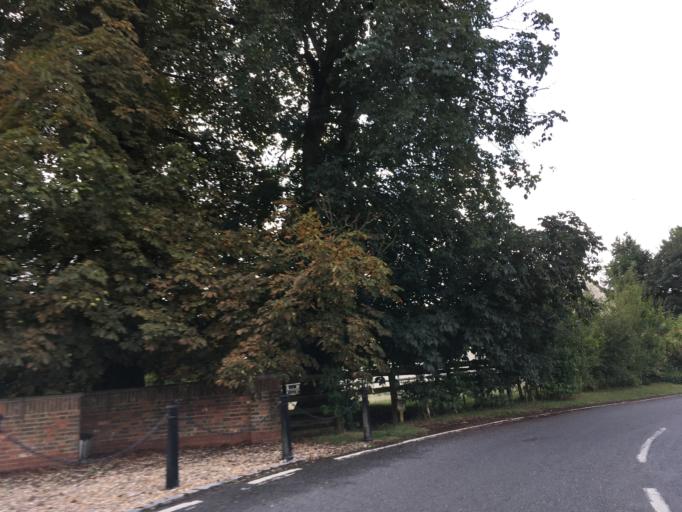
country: GB
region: England
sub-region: Hampshire
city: Andover
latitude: 51.2015
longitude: -1.3786
